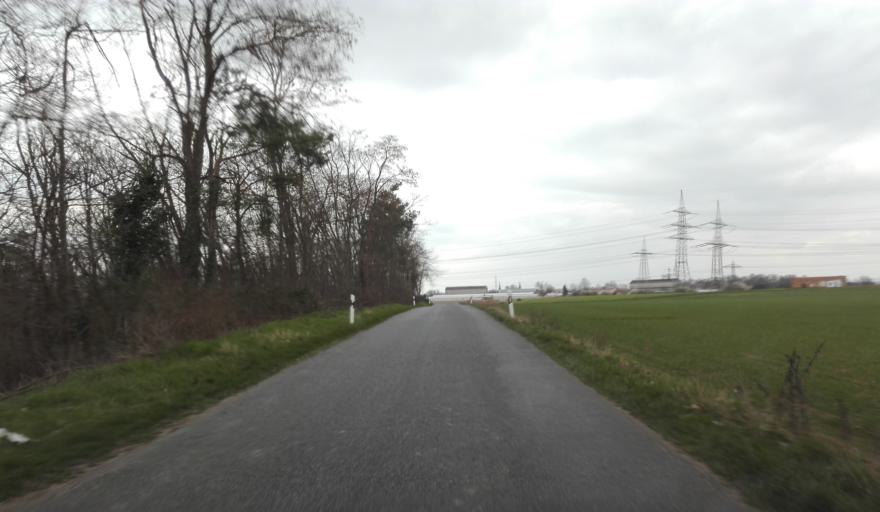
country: DE
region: Baden-Wuerttemberg
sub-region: Karlsruhe Region
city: Plankstadt
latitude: 49.4236
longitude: 8.5784
